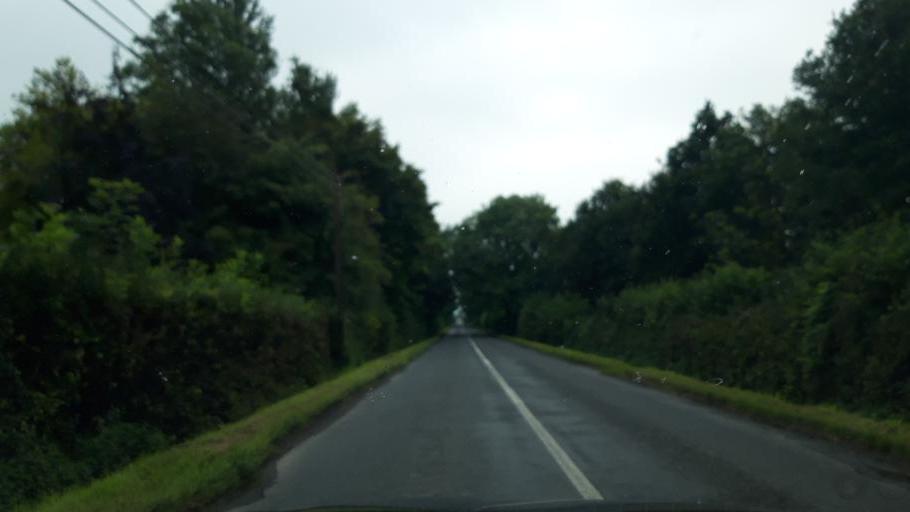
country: IE
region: Munster
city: Fethard
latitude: 52.5011
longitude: -7.6867
